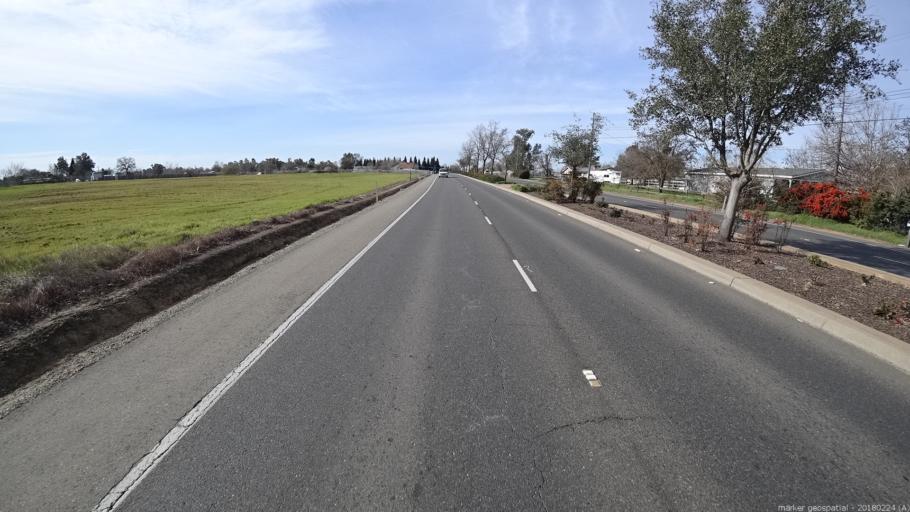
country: US
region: California
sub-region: Sacramento County
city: Rio Linda
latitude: 38.6874
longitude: -121.4306
